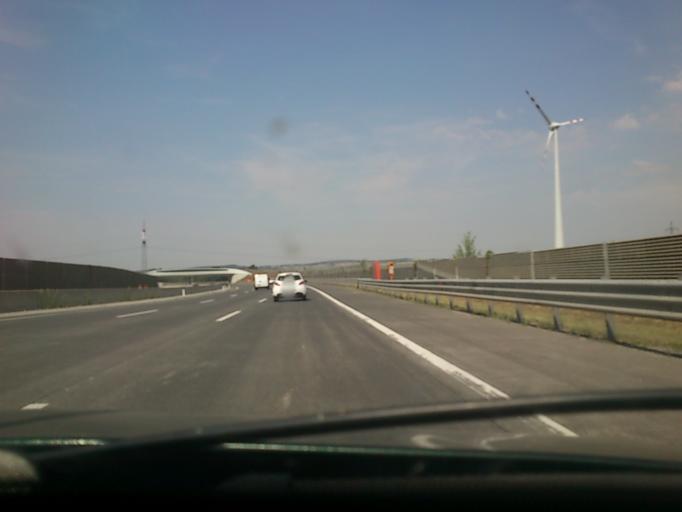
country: AT
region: Lower Austria
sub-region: Politischer Bezirk Mistelbach
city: Grossebersdorf
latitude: 48.3451
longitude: 16.4950
